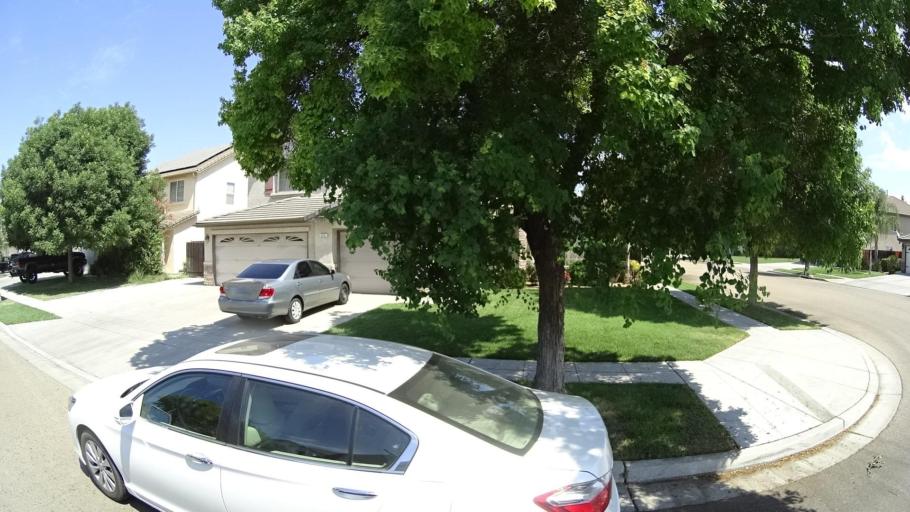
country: US
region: California
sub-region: Fresno County
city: Sunnyside
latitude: 36.7228
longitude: -119.7122
